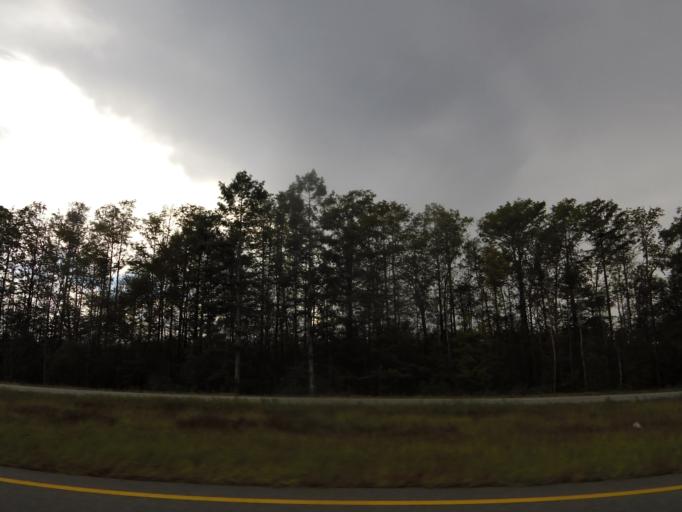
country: US
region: Georgia
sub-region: McIntosh County
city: Darien
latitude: 31.3775
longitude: -81.6309
